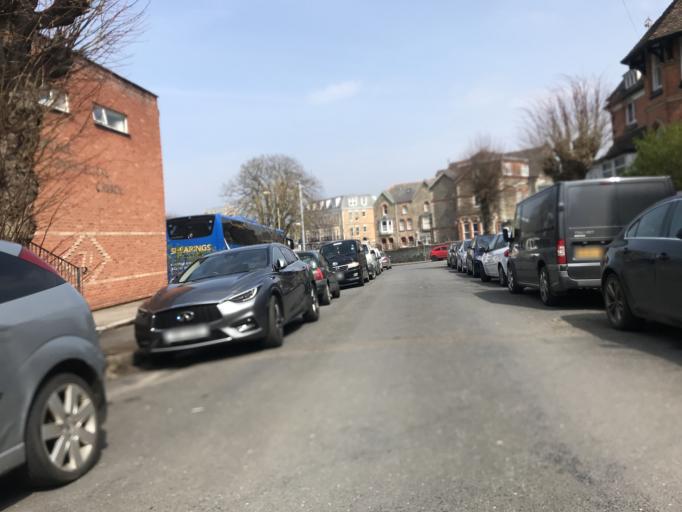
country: GB
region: England
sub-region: Devon
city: Ilfracombe
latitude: 51.2070
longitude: -4.1285
